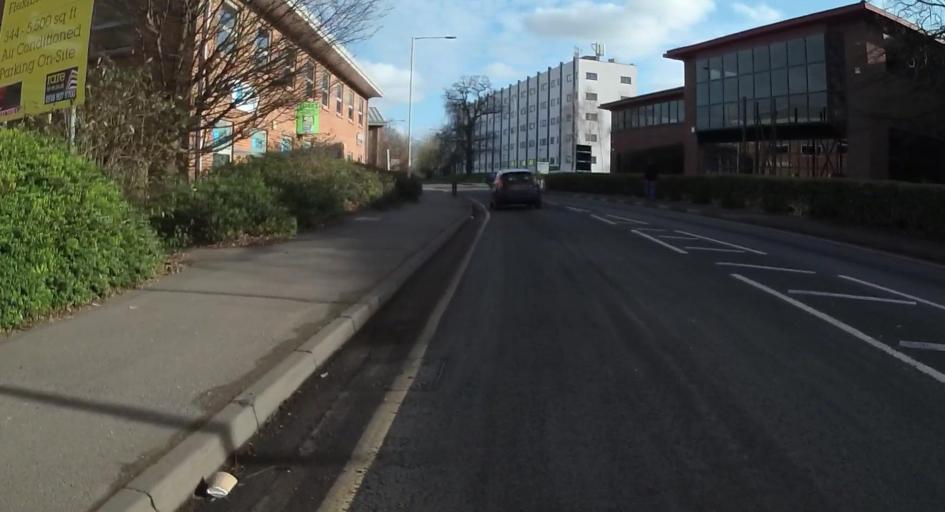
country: GB
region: England
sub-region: Wokingham
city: Wokingham
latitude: 51.4047
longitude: -0.8447
